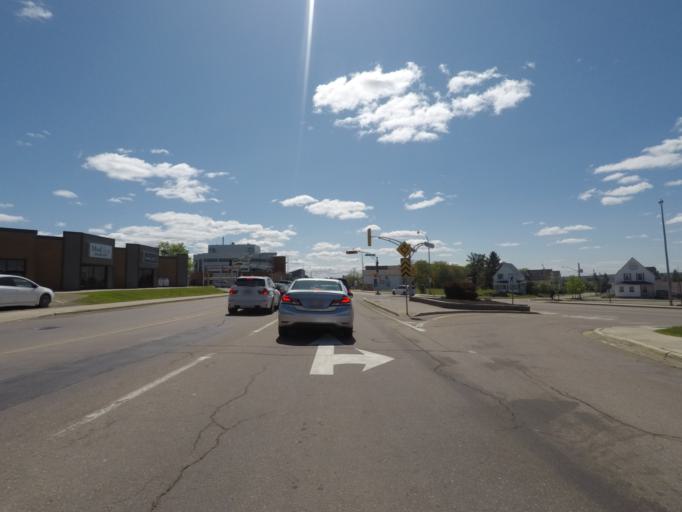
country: CA
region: New Brunswick
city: Moncton
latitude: 46.0954
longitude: -64.7510
